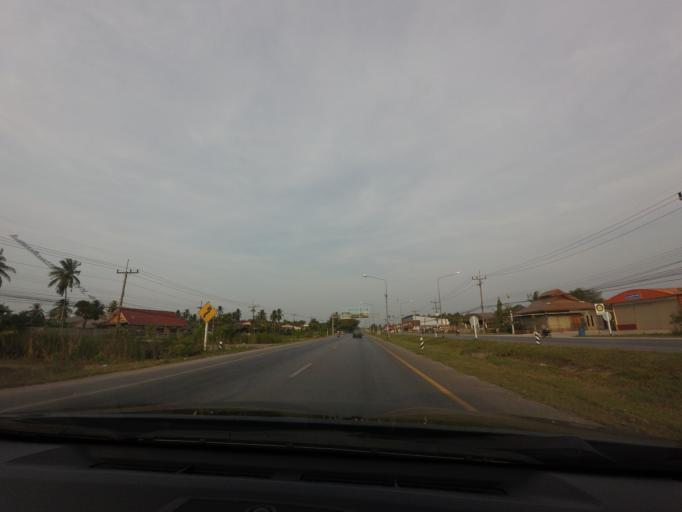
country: TH
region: Pattani
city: Pattani
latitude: 6.8715
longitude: 101.2887
